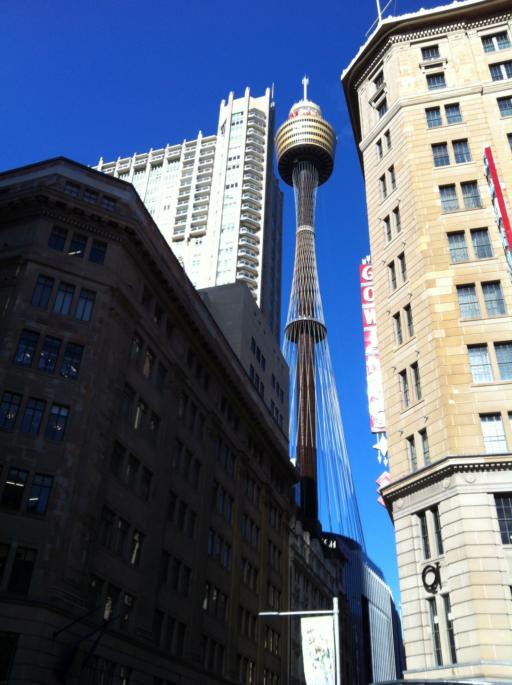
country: AU
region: New South Wales
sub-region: City of Sydney
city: Sydney
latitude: -33.8709
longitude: 151.2069
